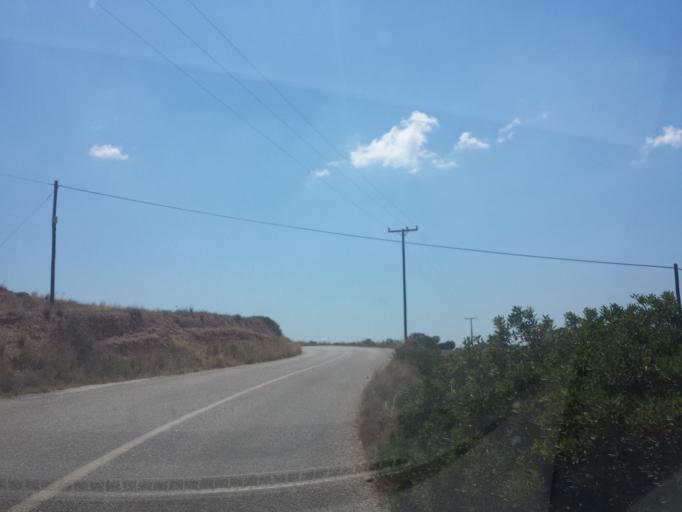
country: GR
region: South Aegean
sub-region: Nomos Kykladon
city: Adamas
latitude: 36.6842
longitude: 24.5054
